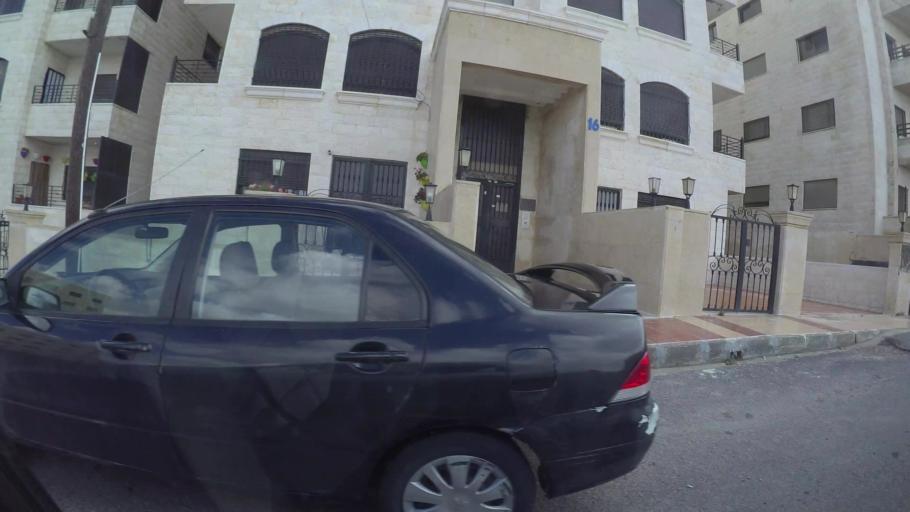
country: JO
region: Amman
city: Al Jubayhah
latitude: 32.0633
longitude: 35.8742
